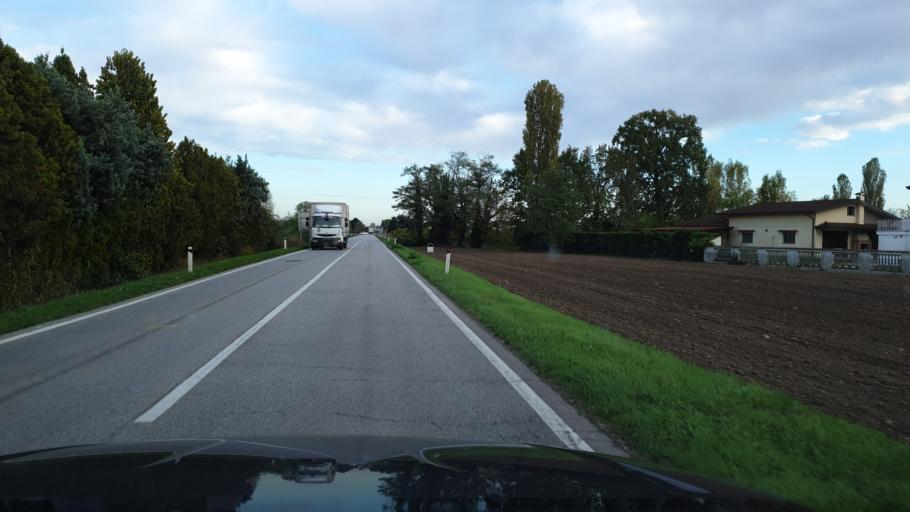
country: IT
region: Veneto
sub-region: Provincia di Padova
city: San Pietro Viminario
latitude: 45.2301
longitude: 11.8079
